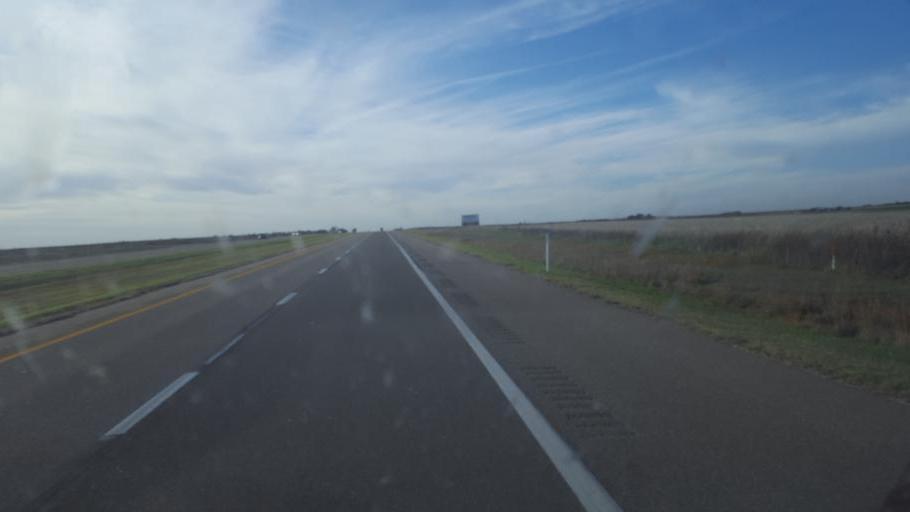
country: US
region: Kansas
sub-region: Trego County
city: WaKeeney
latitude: 39.0267
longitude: -100.1750
